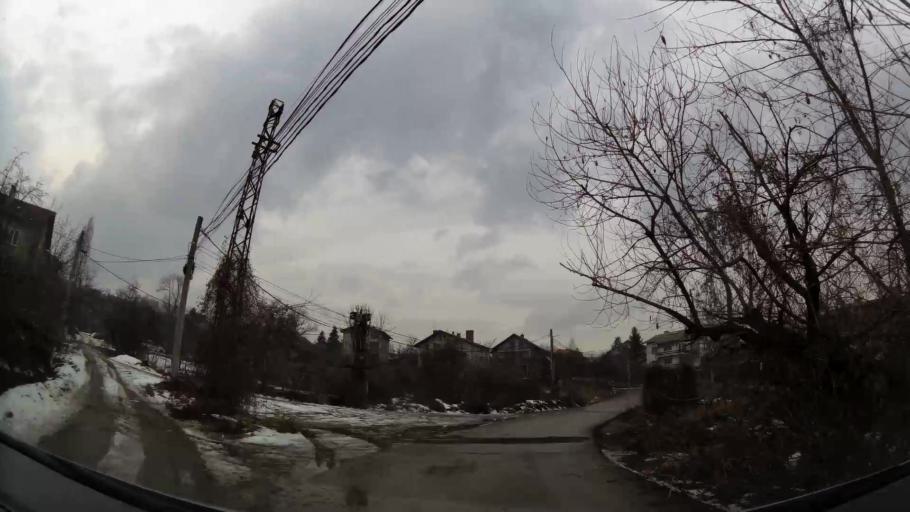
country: BG
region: Sofiya
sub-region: Obshtina Bozhurishte
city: Bozhurishte
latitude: 42.6815
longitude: 23.2349
